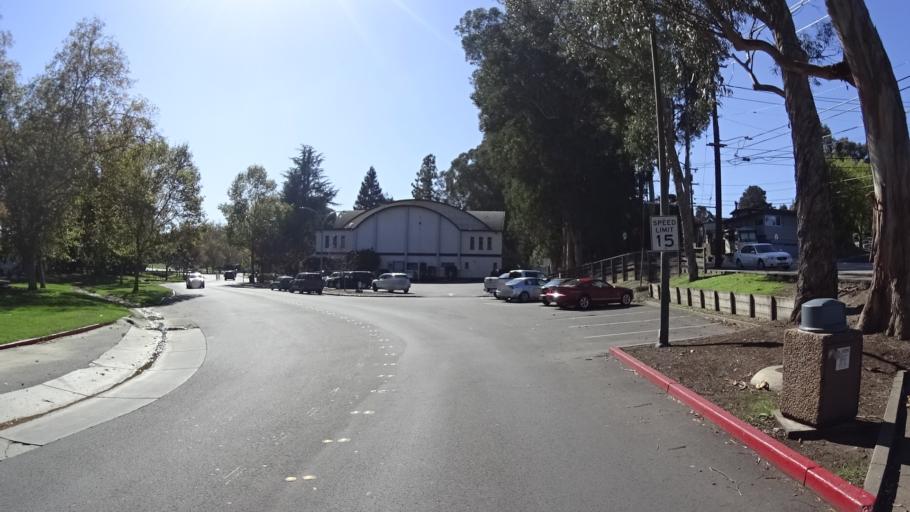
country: US
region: California
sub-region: San Mateo County
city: San Bruno
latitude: 37.6158
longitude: -122.4152
